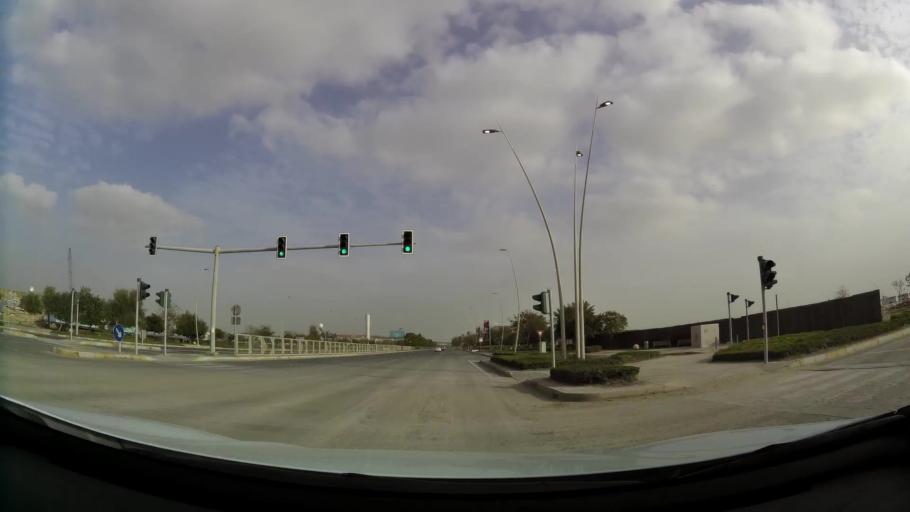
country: AE
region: Abu Dhabi
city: Abu Dhabi
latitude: 24.4899
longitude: 54.5935
